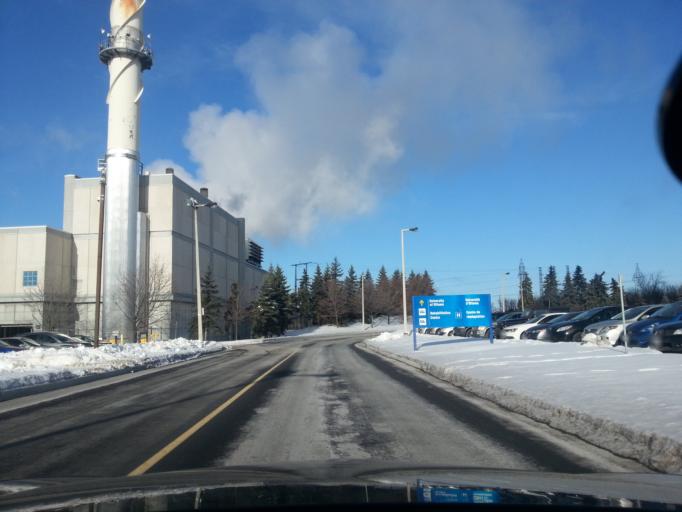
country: CA
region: Ontario
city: Ottawa
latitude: 45.4023
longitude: -75.6537
